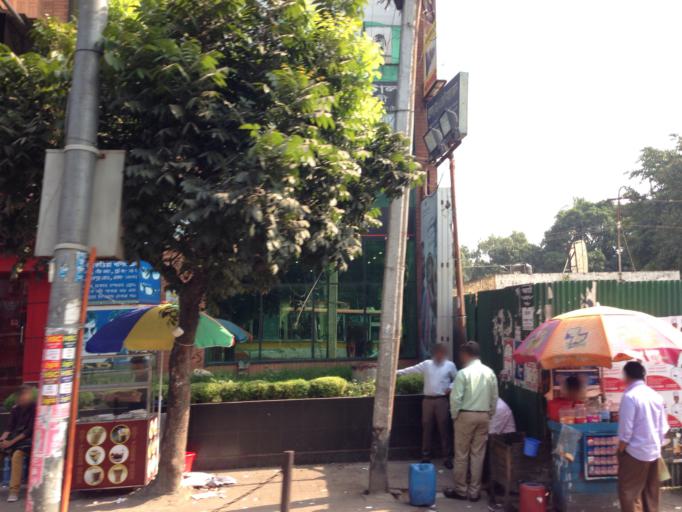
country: BD
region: Dhaka
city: Azimpur
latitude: 23.7413
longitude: 90.3831
